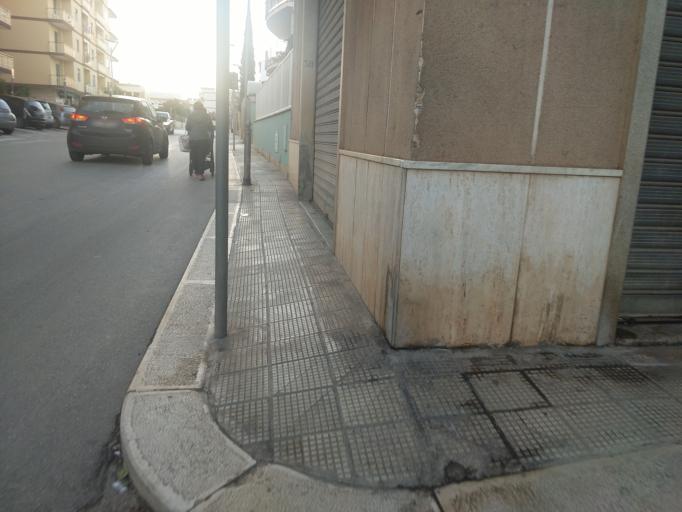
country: IT
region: Apulia
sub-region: Provincia di Bari
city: Modugno
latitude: 41.0780
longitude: 16.7861
